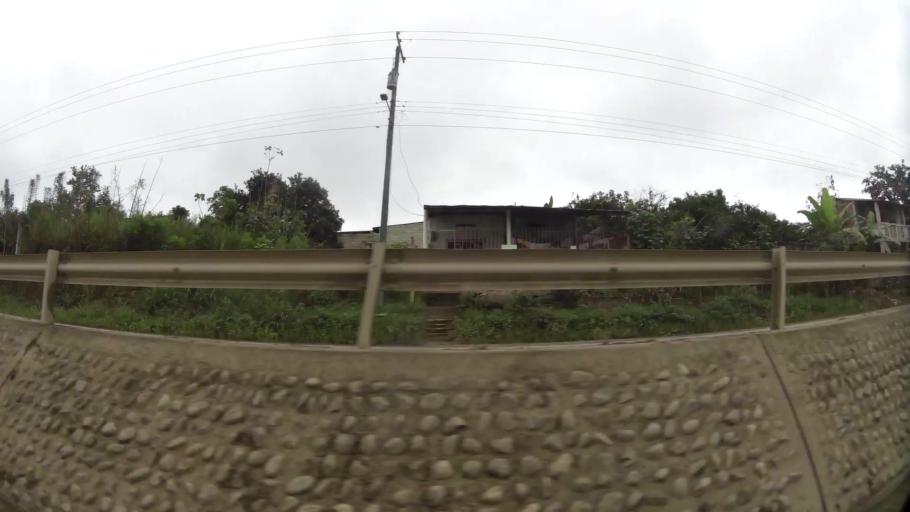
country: EC
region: El Oro
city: Pasaje
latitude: -3.3332
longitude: -79.7869
